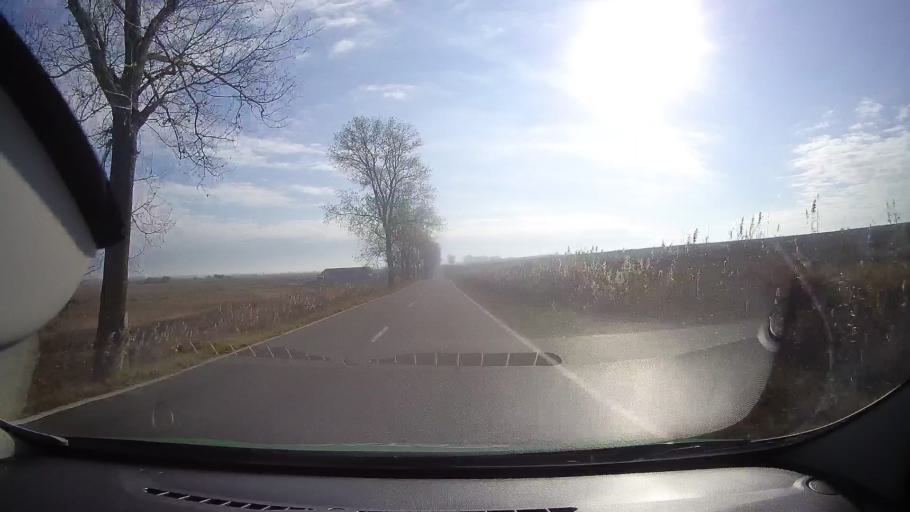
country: RO
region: Tulcea
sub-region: Comuna Mahmudia
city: Mahmudia
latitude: 45.0645
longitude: 29.1093
